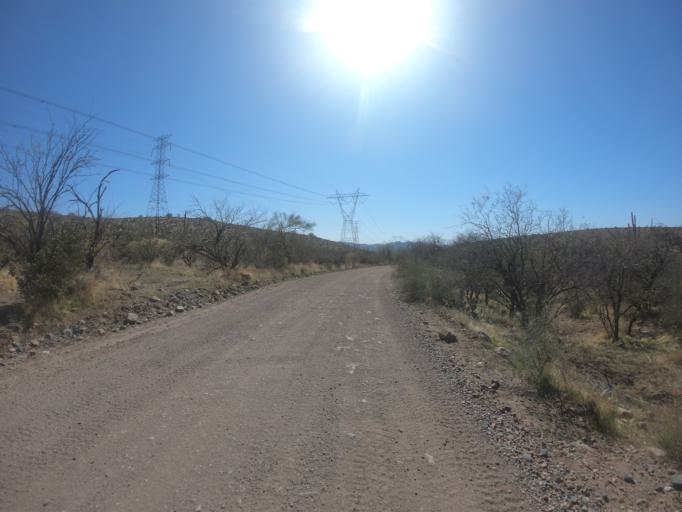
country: US
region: Arizona
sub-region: Pinal County
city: Superior
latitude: 33.2971
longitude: -111.1453
